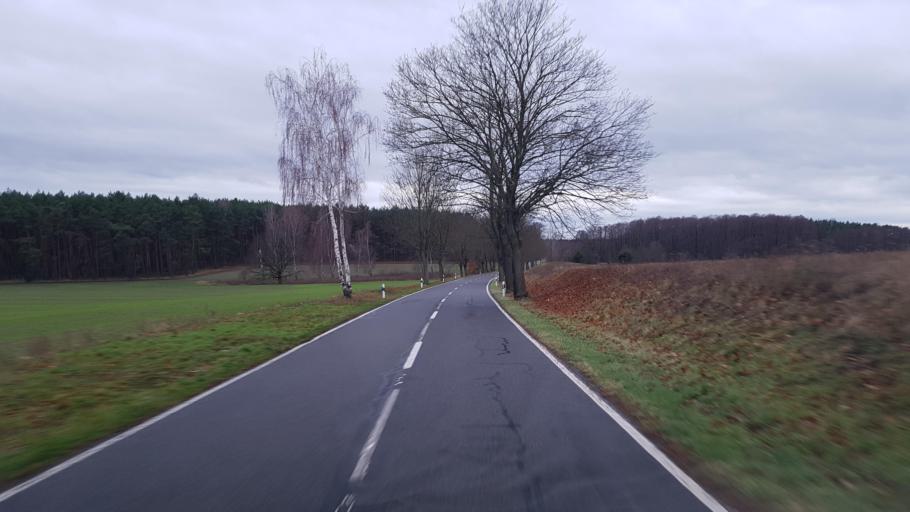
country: DE
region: Brandenburg
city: Wendisch Rietz
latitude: 52.0694
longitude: 14.0412
